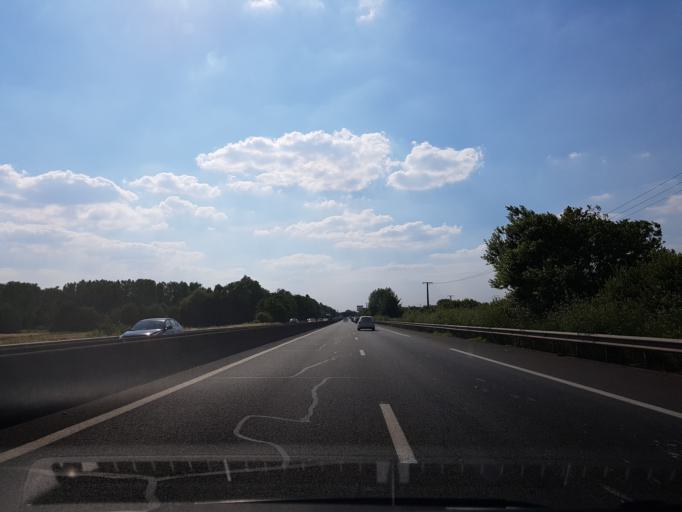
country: FR
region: Nord-Pas-de-Calais
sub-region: Departement du Nord
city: Lallaing
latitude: 50.3789
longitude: 3.1561
